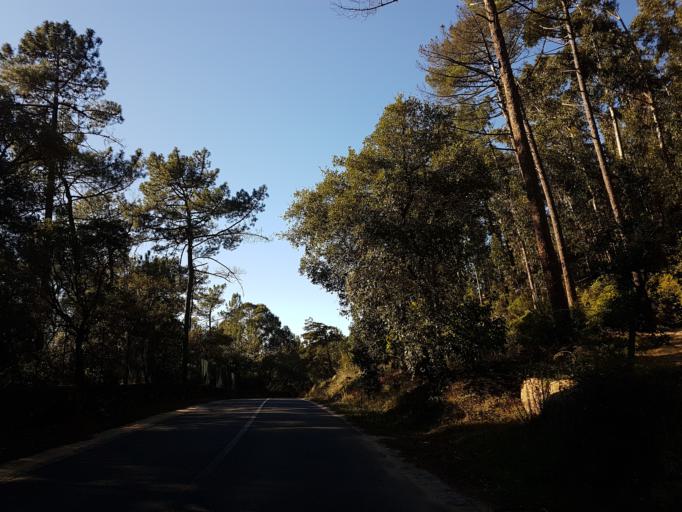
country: PT
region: Lisbon
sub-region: Cascais
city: Alcabideche
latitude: 38.7630
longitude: -9.4032
